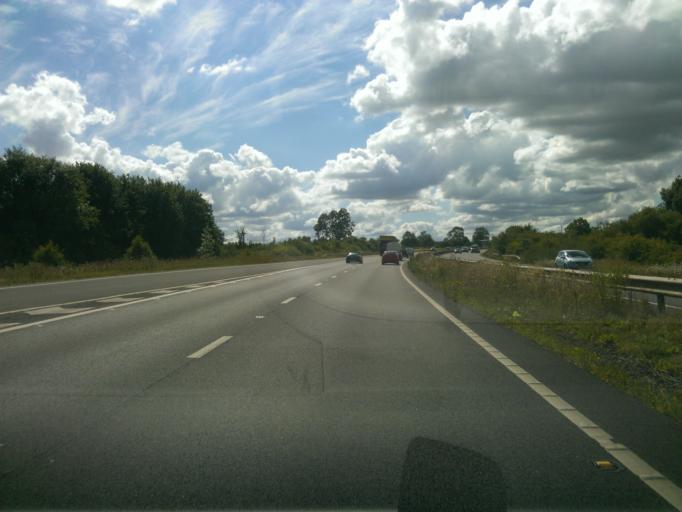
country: GB
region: England
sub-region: Northamptonshire
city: Long Buckby
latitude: 52.3955
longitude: -1.0356
